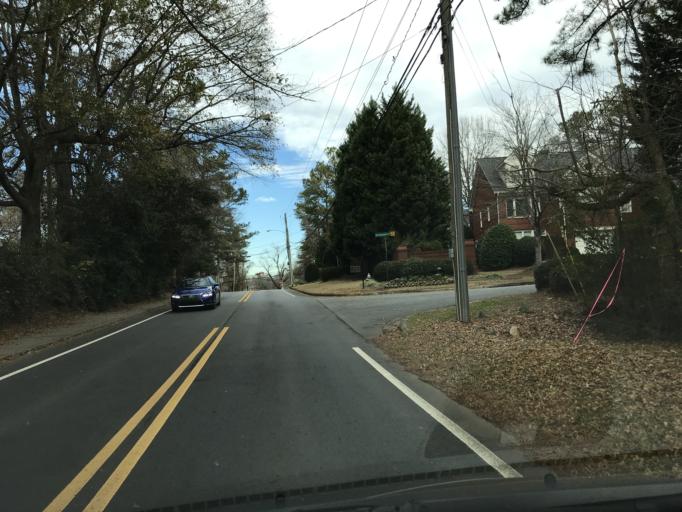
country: US
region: Georgia
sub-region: DeKalb County
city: North Atlanta
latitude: 33.8795
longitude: -84.3422
